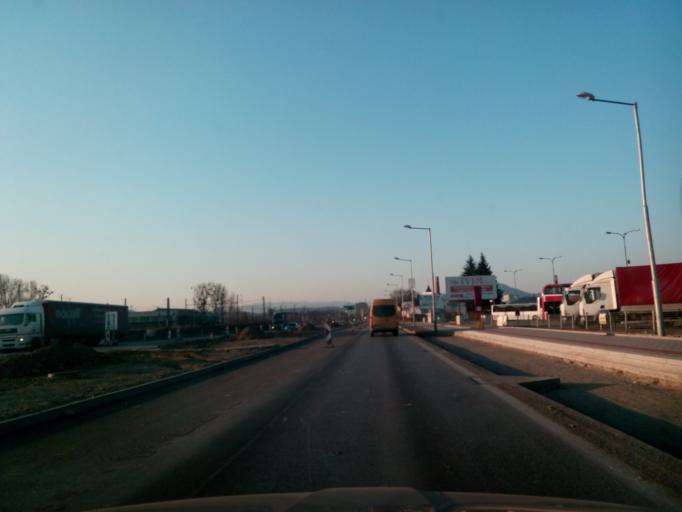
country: SK
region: Presovsky
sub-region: Okres Presov
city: Presov
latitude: 48.9727
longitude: 21.2529
